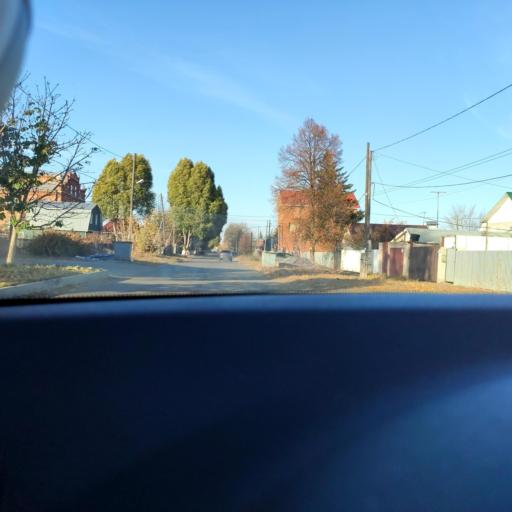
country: RU
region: Samara
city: Petra-Dubrava
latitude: 53.2504
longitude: 50.3285
